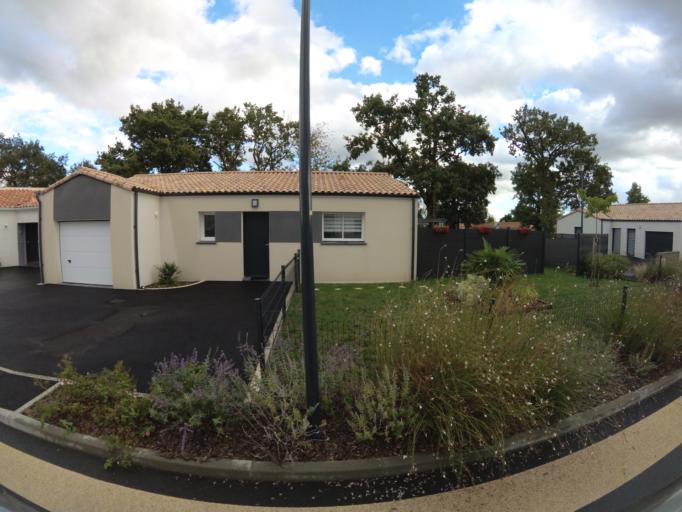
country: FR
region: Pays de la Loire
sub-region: Departement de la Loire-Atlantique
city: Saint-Lumine-de-Clisson
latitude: 47.0885
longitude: -1.3341
